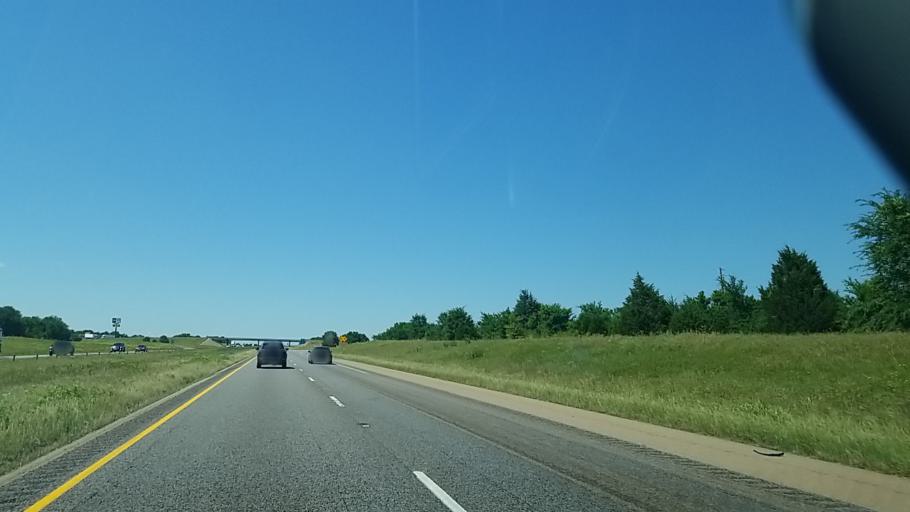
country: US
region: Texas
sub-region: Freestone County
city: Fairfield
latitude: 31.5917
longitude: -96.1521
